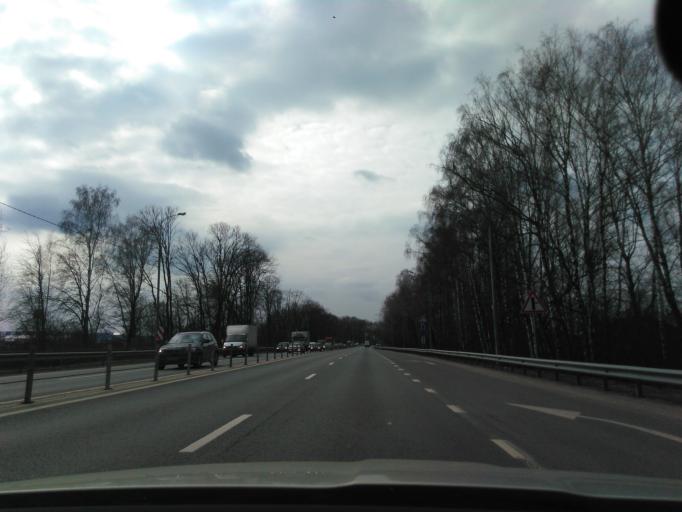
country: RU
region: Moskovskaya
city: Marfino
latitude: 56.0176
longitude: 37.5455
